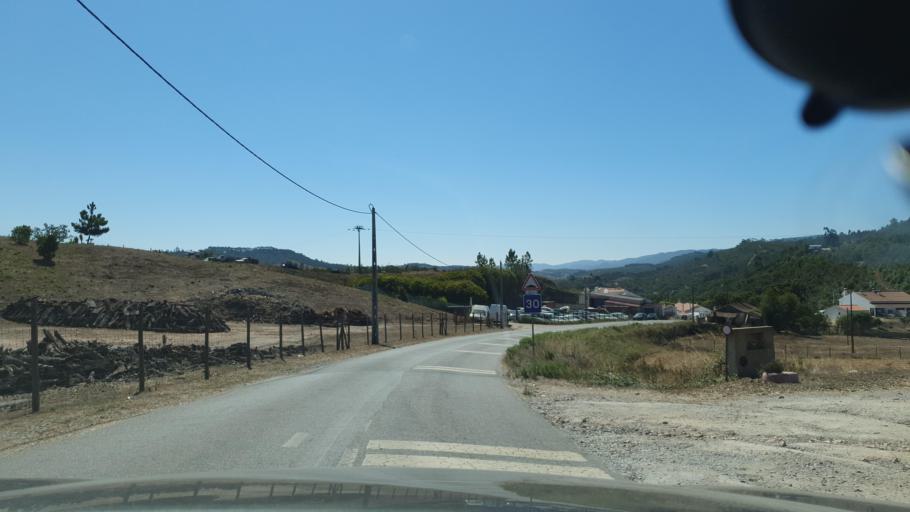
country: PT
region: Beja
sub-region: Odemira
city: Sao Teotonio
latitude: 37.5015
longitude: -8.6558
